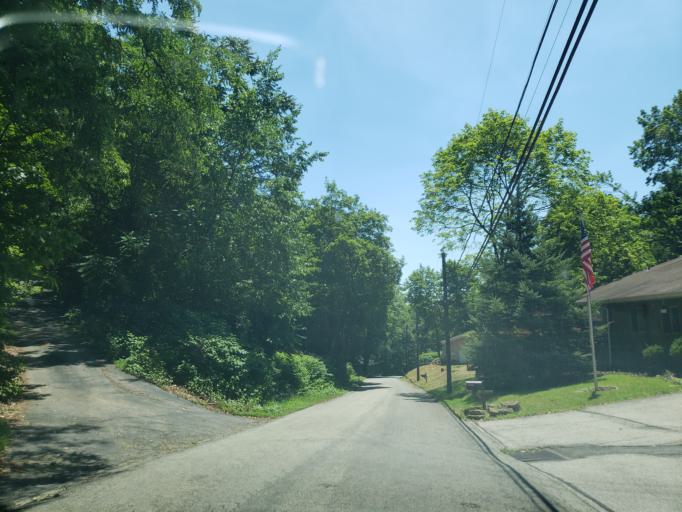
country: US
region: Pennsylvania
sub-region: Allegheny County
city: Emsworth
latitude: 40.5172
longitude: -80.0968
